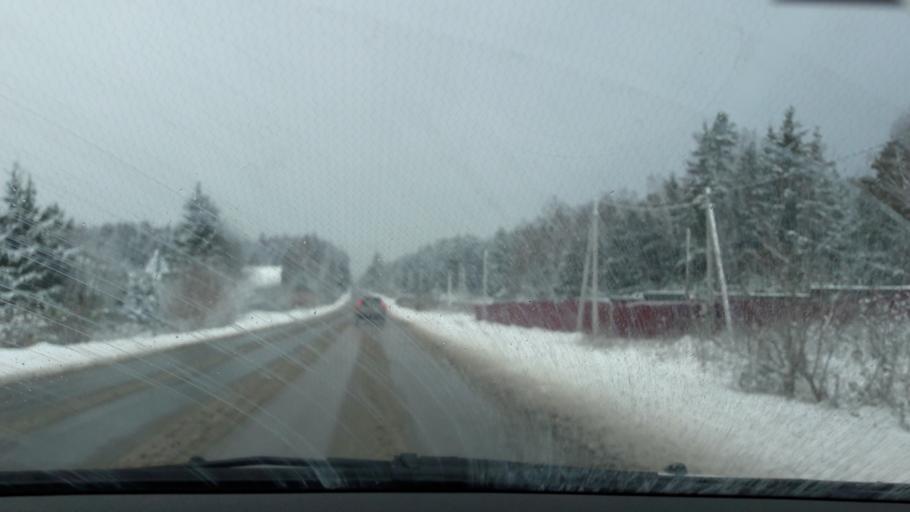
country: RU
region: Moskovskaya
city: Zvenigorod
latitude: 55.6373
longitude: 36.8504
